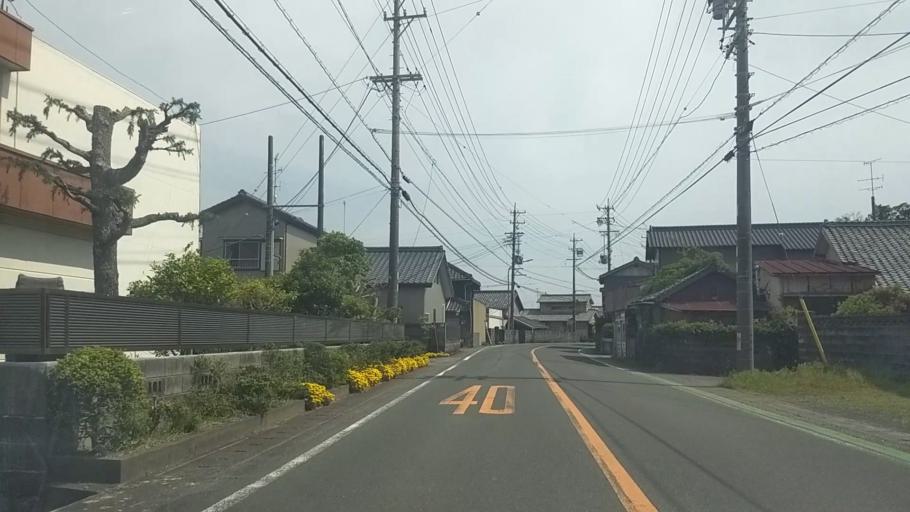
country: JP
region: Shizuoka
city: Kosai-shi
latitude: 34.7420
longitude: 137.6038
